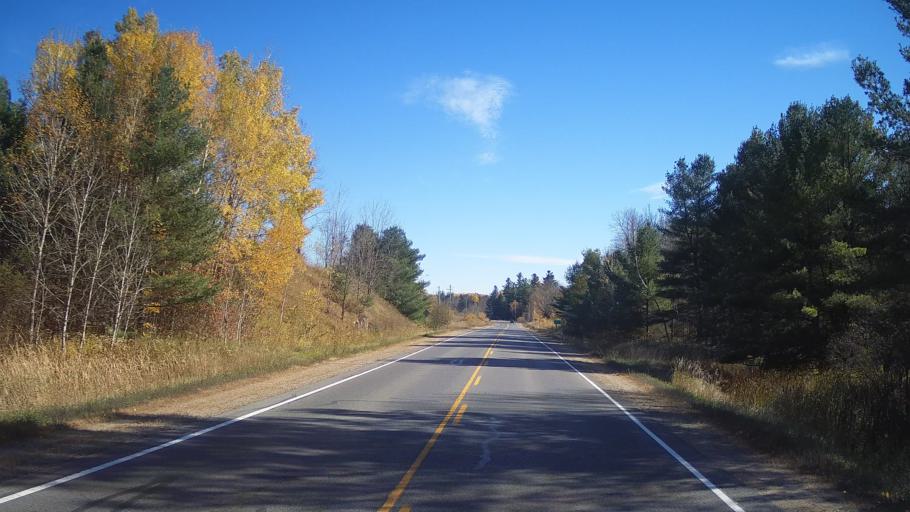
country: CA
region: Ontario
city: Skatepark
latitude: 44.6331
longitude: -76.7117
